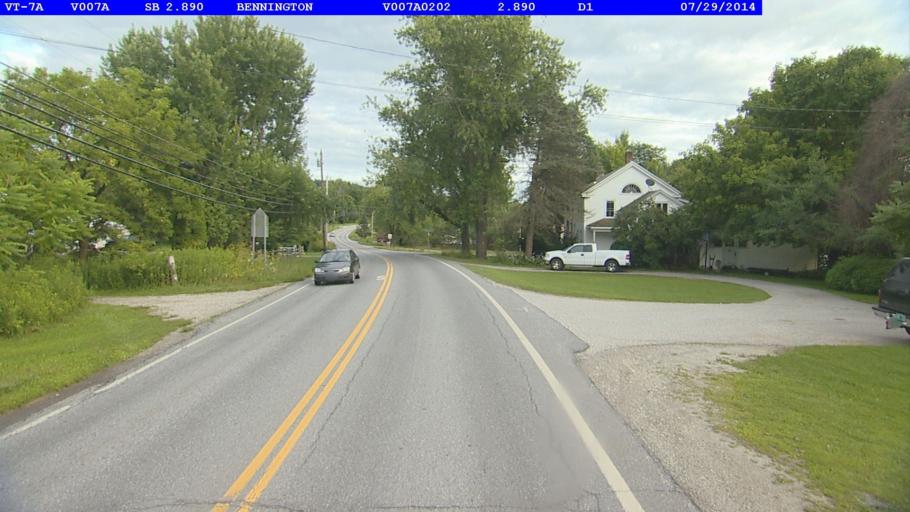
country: US
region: Vermont
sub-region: Bennington County
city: North Bennington
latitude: 42.9308
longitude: -73.2100
